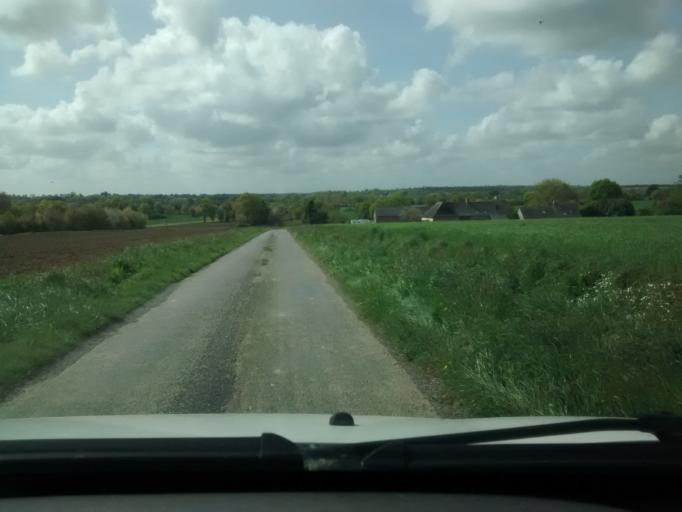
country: FR
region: Brittany
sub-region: Departement d'Ille-et-Vilaine
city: Chantepie
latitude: 48.0927
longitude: -1.5909
